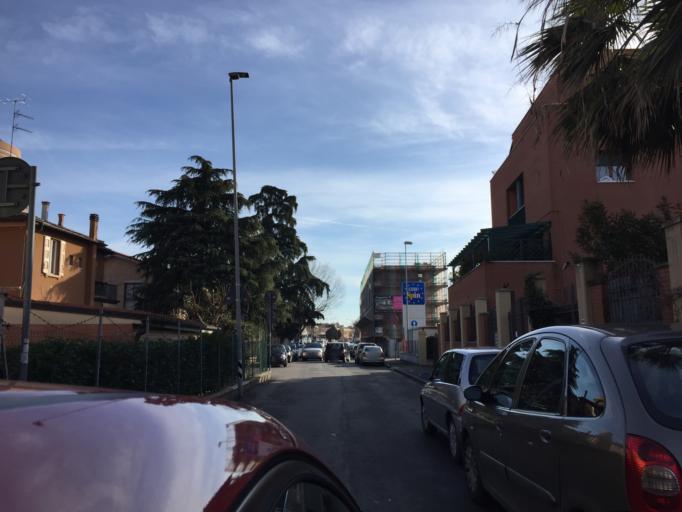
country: IT
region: Emilia-Romagna
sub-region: Provincia di Bologna
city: Bologna
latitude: 44.5041
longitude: 11.3018
